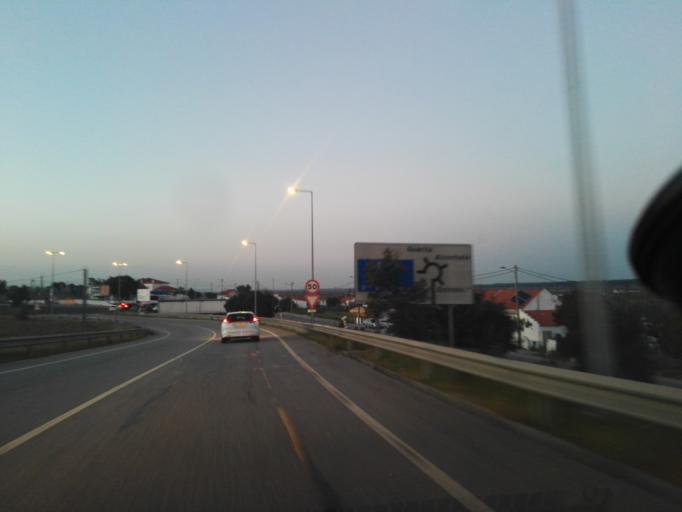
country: PT
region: Setubal
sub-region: Alcochete
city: Alcochete
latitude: 38.7441
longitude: -8.9292
